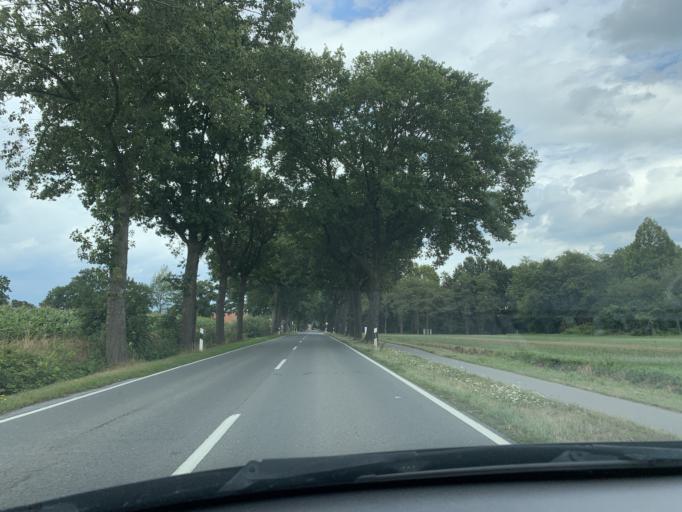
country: DE
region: Lower Saxony
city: Westerstede
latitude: 53.2409
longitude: 7.9191
